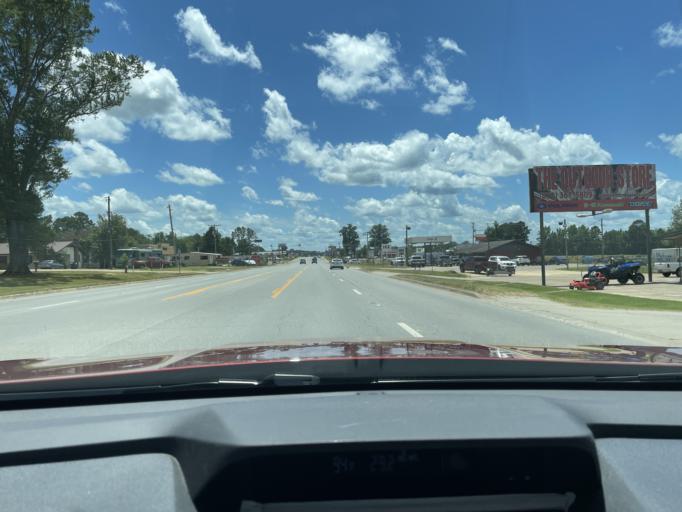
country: US
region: Arkansas
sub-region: Drew County
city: Monticello
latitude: 33.6423
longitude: -91.8010
